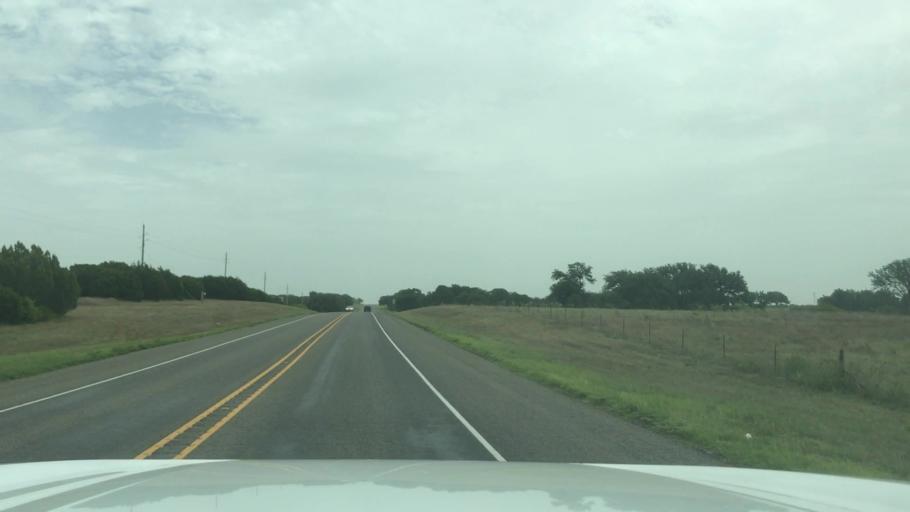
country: US
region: Texas
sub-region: Hamilton County
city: Hico
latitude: 31.9811
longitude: -98.0110
